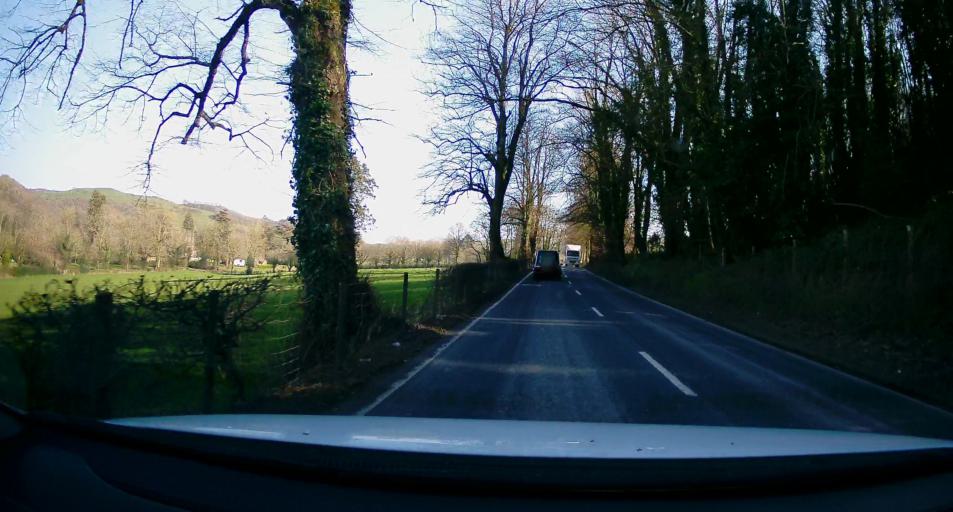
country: GB
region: Wales
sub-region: County of Ceredigion
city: Penparcau
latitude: 52.3650
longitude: -4.0619
